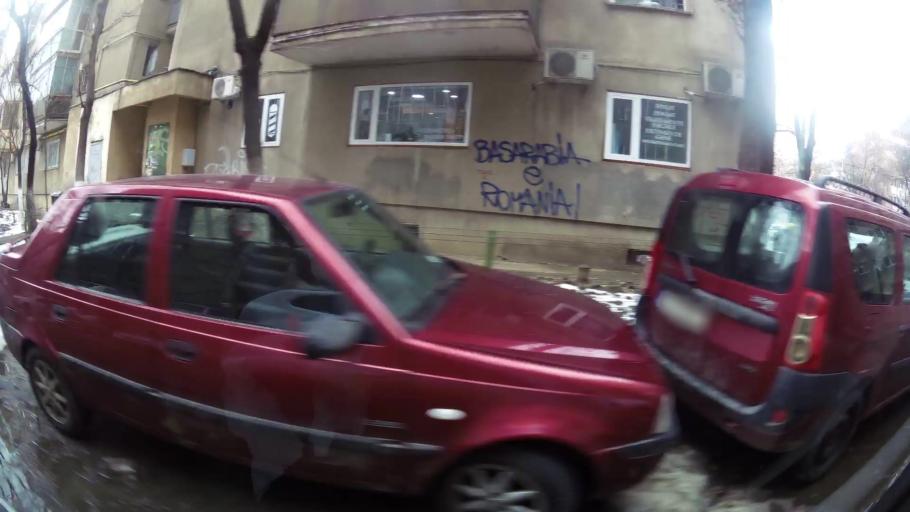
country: RO
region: Ilfov
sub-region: Comuna Chiajna
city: Rosu
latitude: 44.4189
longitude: 26.0468
